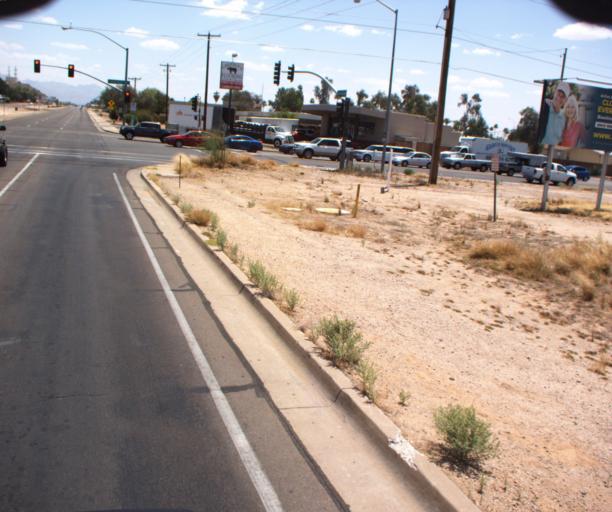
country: US
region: Arizona
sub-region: Pinal County
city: Apache Junction
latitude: 33.4151
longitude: -111.6680
